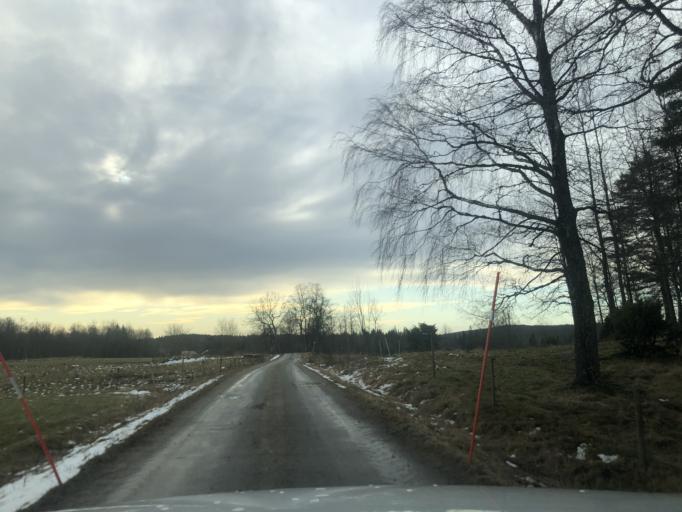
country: SE
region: Vaestra Goetaland
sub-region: Ulricehamns Kommun
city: Ulricehamn
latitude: 57.7976
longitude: 13.4901
